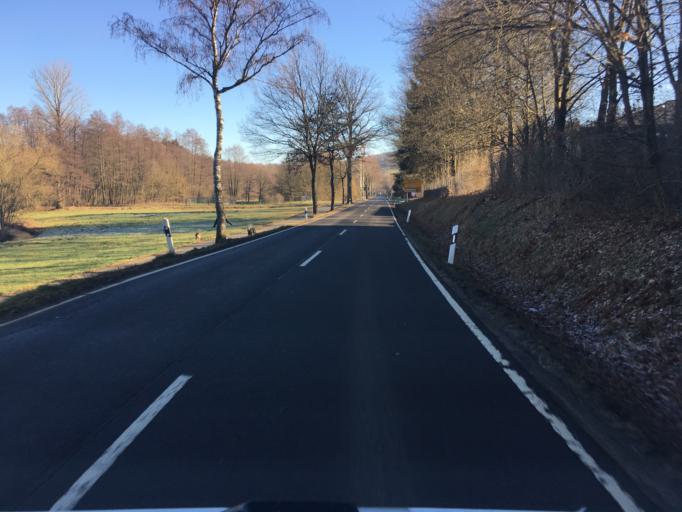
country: DE
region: North Rhine-Westphalia
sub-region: Regierungsbezirk Koln
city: Numbrecht
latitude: 50.9209
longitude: 7.5668
